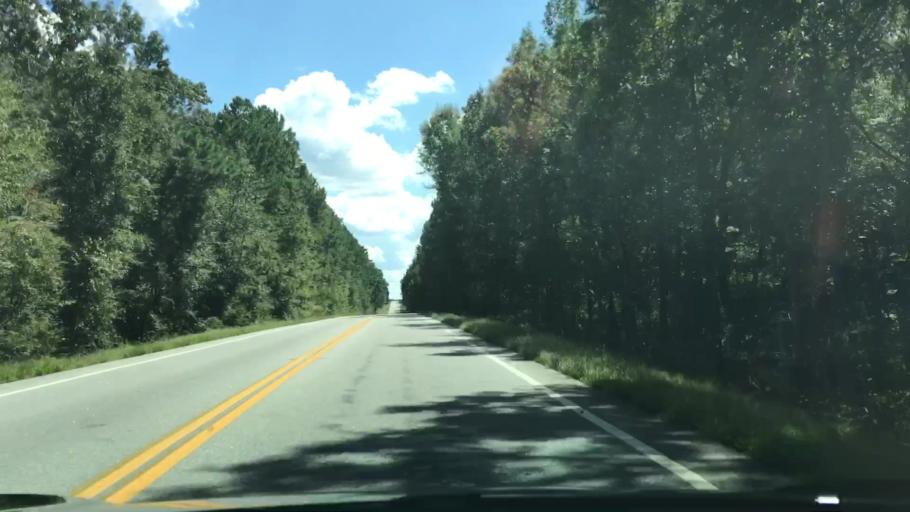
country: US
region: Georgia
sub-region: Greene County
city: Greensboro
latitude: 33.6284
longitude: -83.2149
